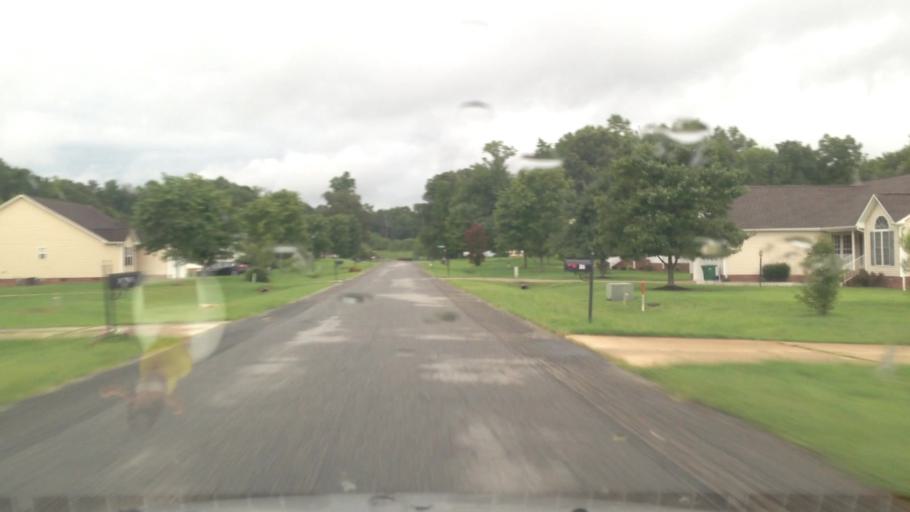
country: US
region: North Carolina
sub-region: Rockingham County
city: Reidsville
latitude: 36.2652
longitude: -79.7187
